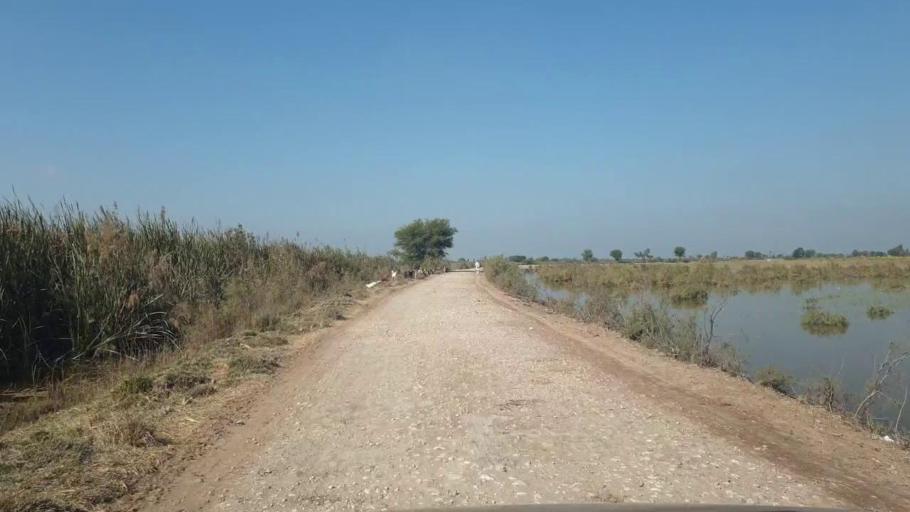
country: PK
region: Sindh
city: Bhit Shah
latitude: 25.8751
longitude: 68.5287
